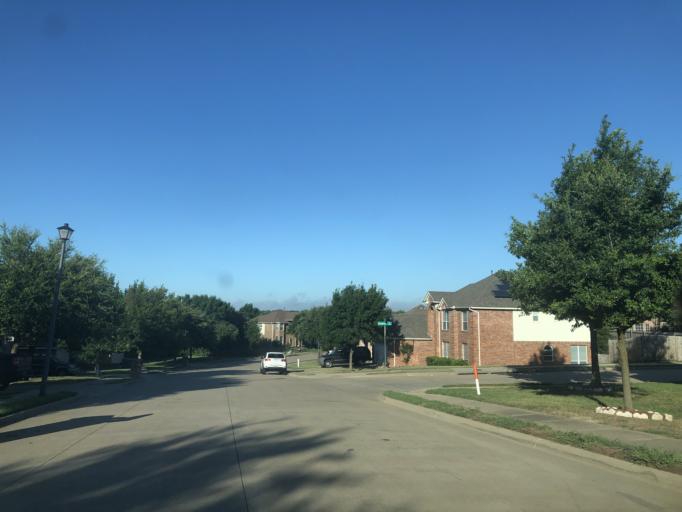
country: US
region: Texas
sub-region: Dallas County
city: Duncanville
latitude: 32.6577
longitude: -96.9490
